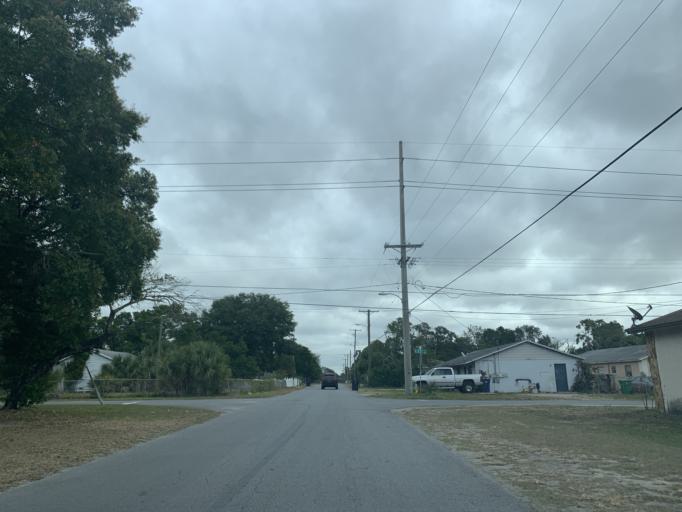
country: US
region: Florida
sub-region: Hillsborough County
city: East Lake-Orient Park
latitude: 27.9760
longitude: -82.3981
